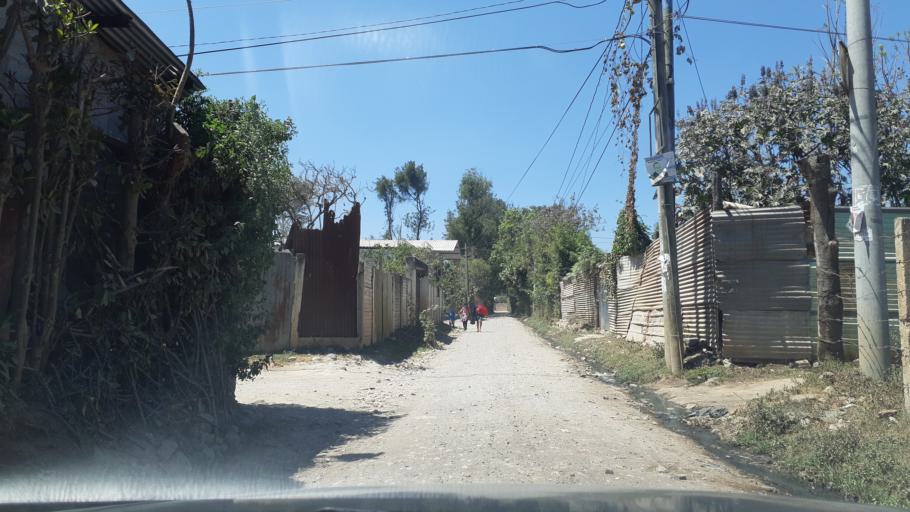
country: GT
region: Chimaltenango
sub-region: Municipio de Chimaltenango
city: Chimaltenango
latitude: 14.6523
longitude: -90.8091
